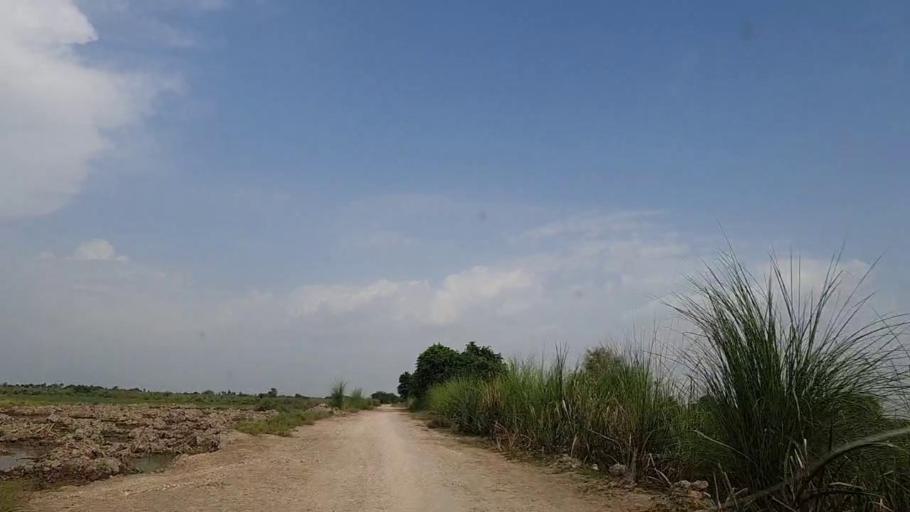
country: PK
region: Sindh
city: Khanpur
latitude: 27.8232
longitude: 69.5222
